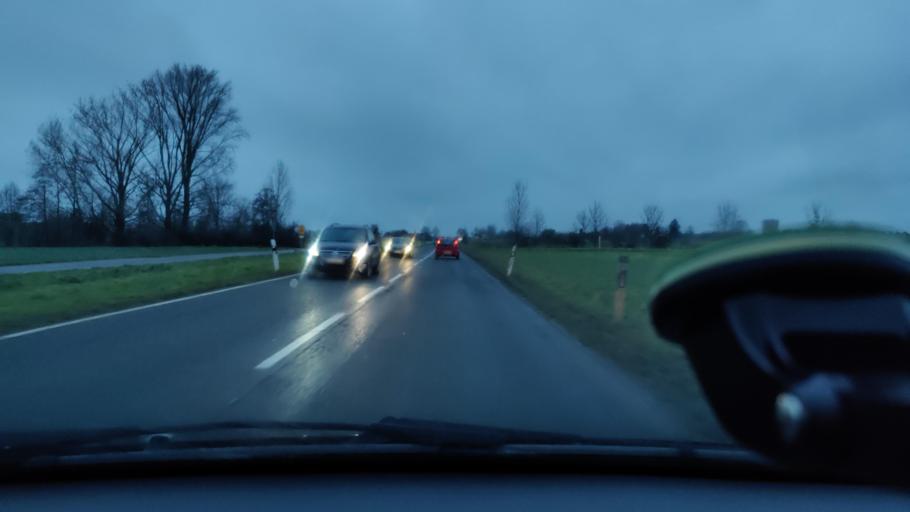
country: DE
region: North Rhine-Westphalia
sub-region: Regierungsbezirk Dusseldorf
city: Xanten
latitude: 51.6650
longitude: 6.4324
